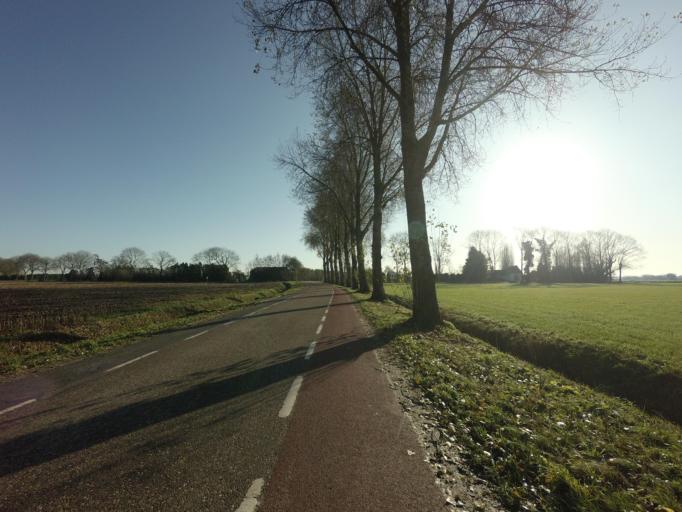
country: NL
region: Gelderland
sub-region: Gemeente Zaltbommel
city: Zaltbommel
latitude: 51.7934
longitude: 5.2692
